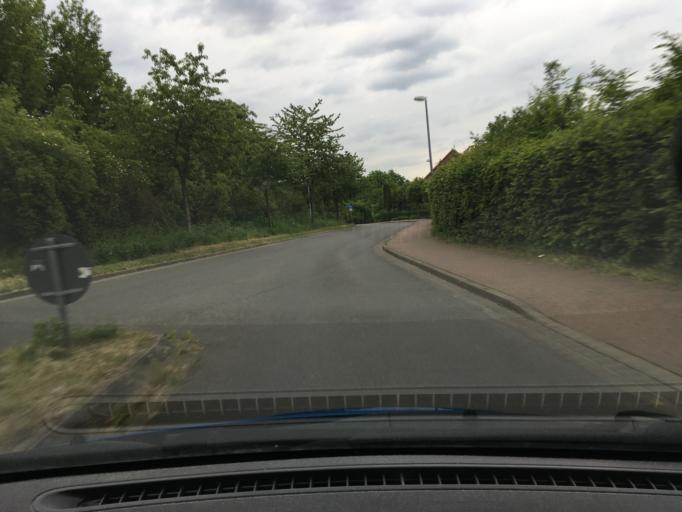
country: DE
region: Lower Saxony
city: Lueneburg
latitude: 53.2504
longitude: 10.3857
